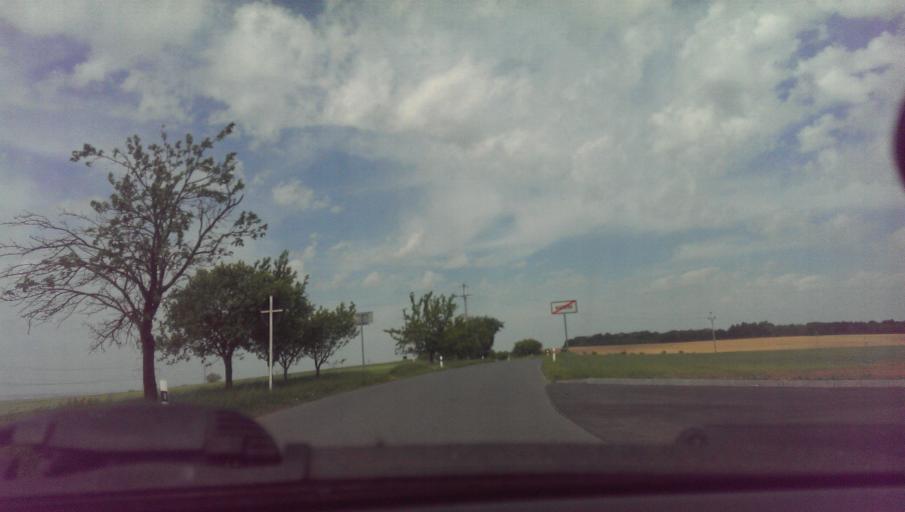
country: CZ
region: Zlin
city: Otrokovice
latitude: 49.2528
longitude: 17.5407
